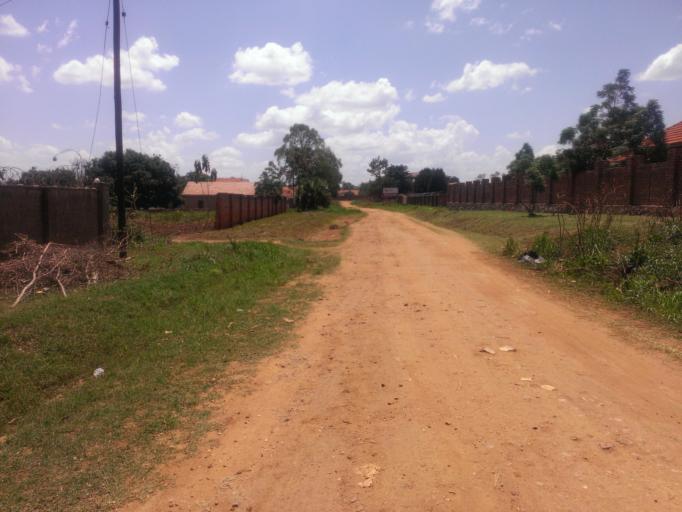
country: UG
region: Northern Region
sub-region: Gulu District
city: Gulu
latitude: 2.7849
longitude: 32.2994
